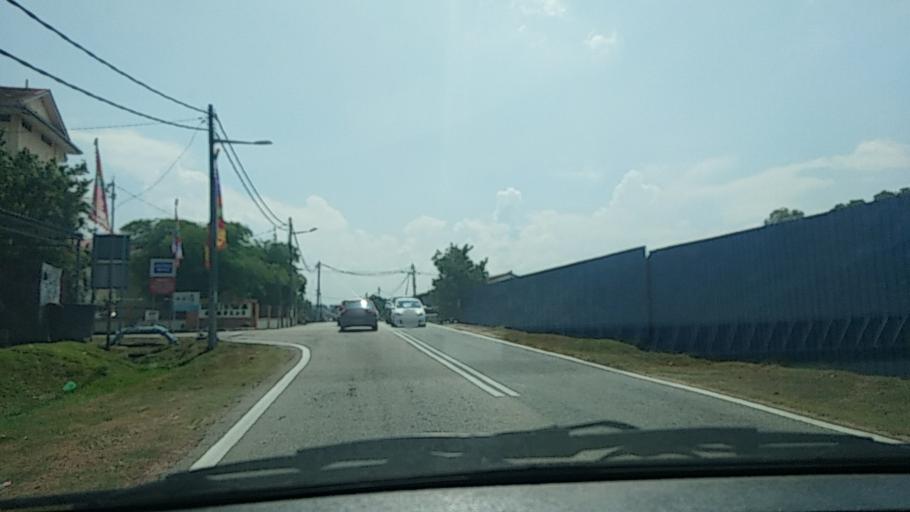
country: MY
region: Kedah
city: Sungai Petani
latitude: 5.6378
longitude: 100.5003
